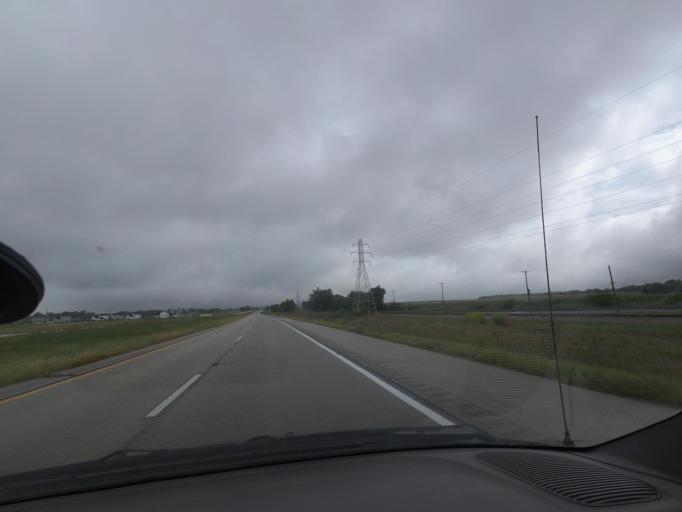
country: US
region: Illinois
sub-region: Piatt County
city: Monticello
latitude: 40.0579
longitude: -88.5568
